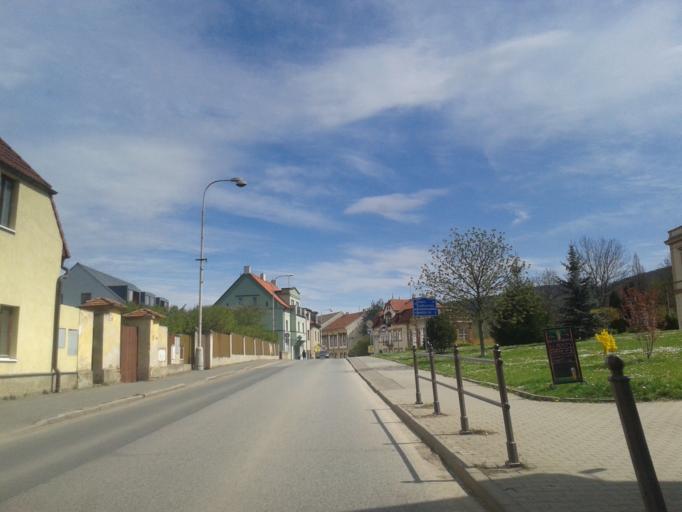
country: CZ
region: Central Bohemia
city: Revnice
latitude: 49.9137
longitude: 14.2331
